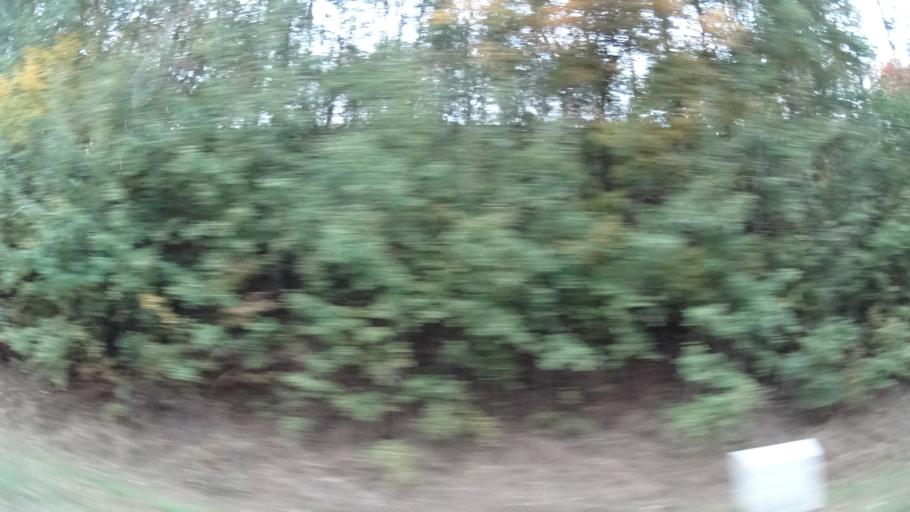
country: DE
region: Hesse
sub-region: Regierungsbezirk Kassel
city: Flieden
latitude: 50.4309
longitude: 9.5866
